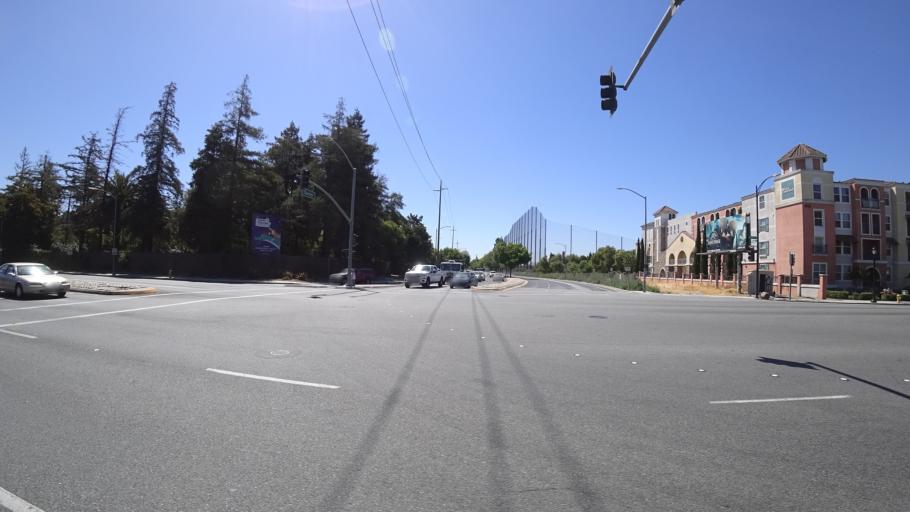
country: US
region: California
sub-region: Santa Clara County
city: San Jose
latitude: 37.3258
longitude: -121.8657
